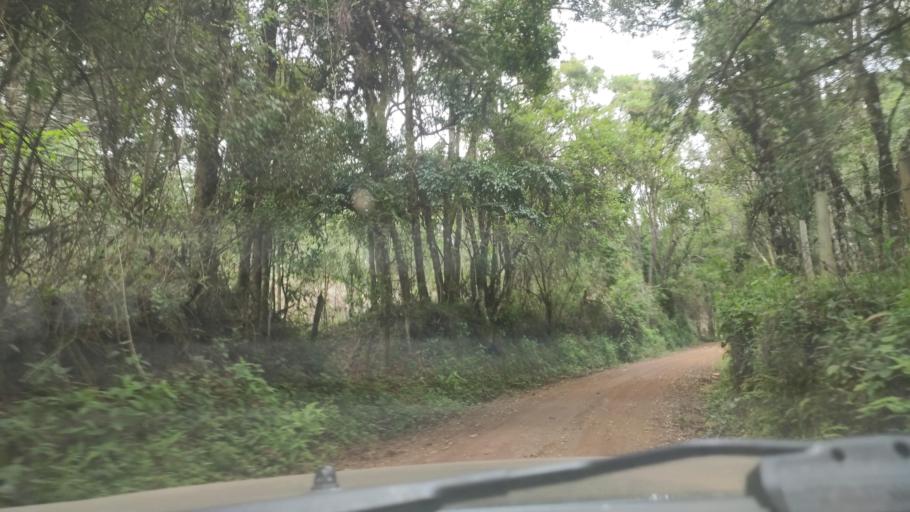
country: BR
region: Minas Gerais
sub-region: Paraisopolis
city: Paraisopolis
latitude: -22.7246
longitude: -45.8409
